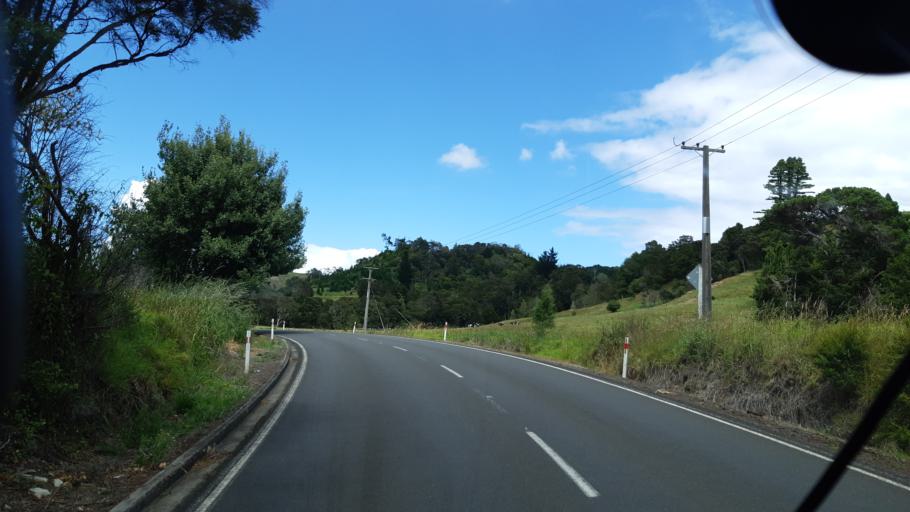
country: NZ
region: Northland
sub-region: Far North District
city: Taipa
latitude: -35.2580
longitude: 173.5296
